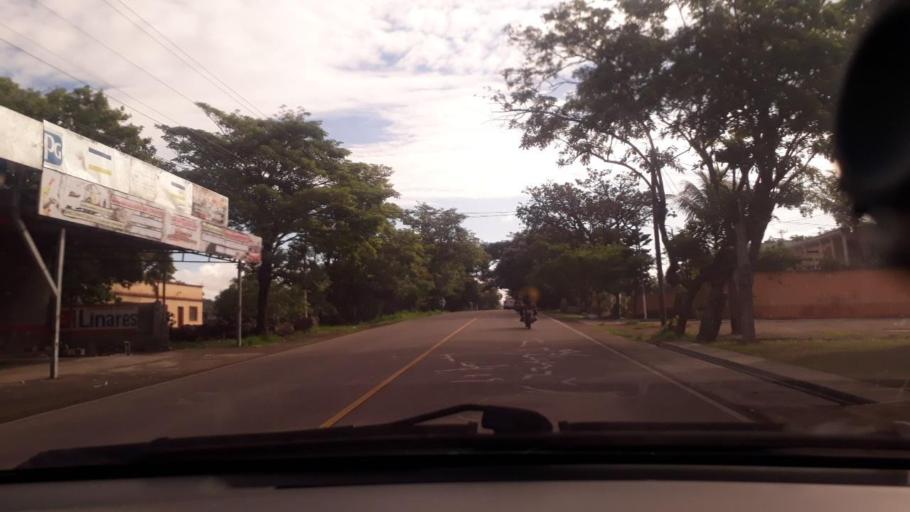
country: GT
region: Jutiapa
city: El Progreso
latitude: 14.3250
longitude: -89.8610
